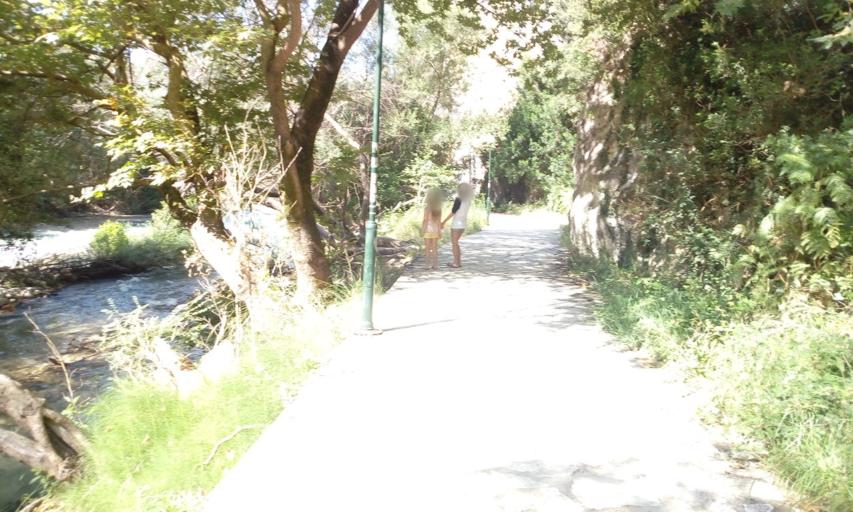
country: GR
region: Epirus
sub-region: Nomos Prevezis
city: Kanalaki
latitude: 39.3287
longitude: 20.6199
